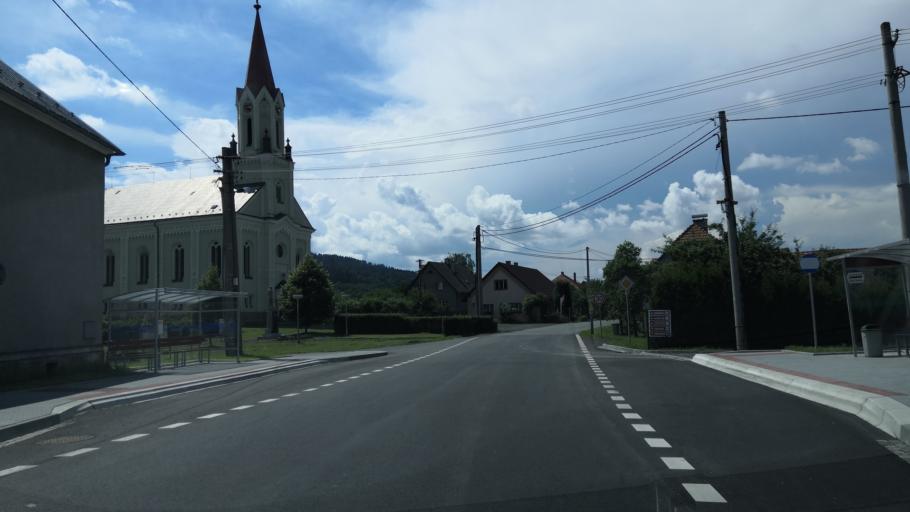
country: CZ
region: Zlin
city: Zasova
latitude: 49.4569
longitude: 18.0647
